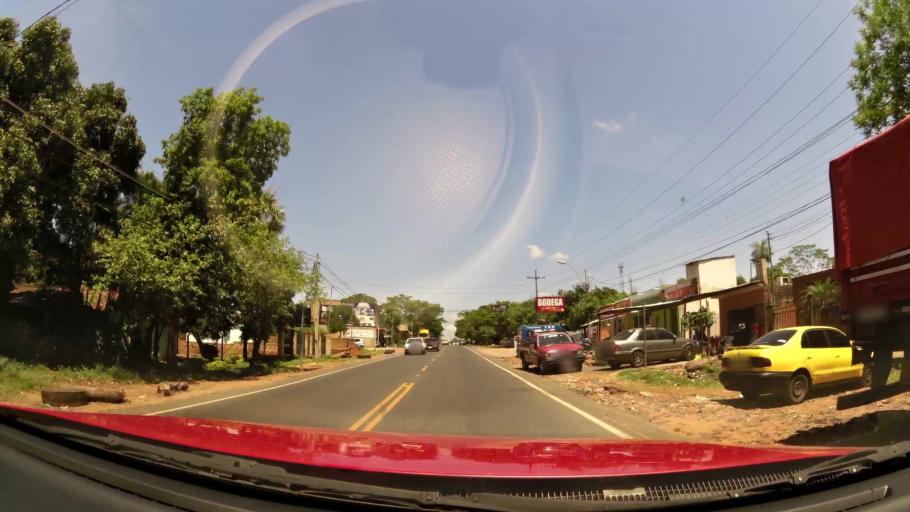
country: PY
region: Central
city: Nemby
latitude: -25.4061
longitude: -57.5439
